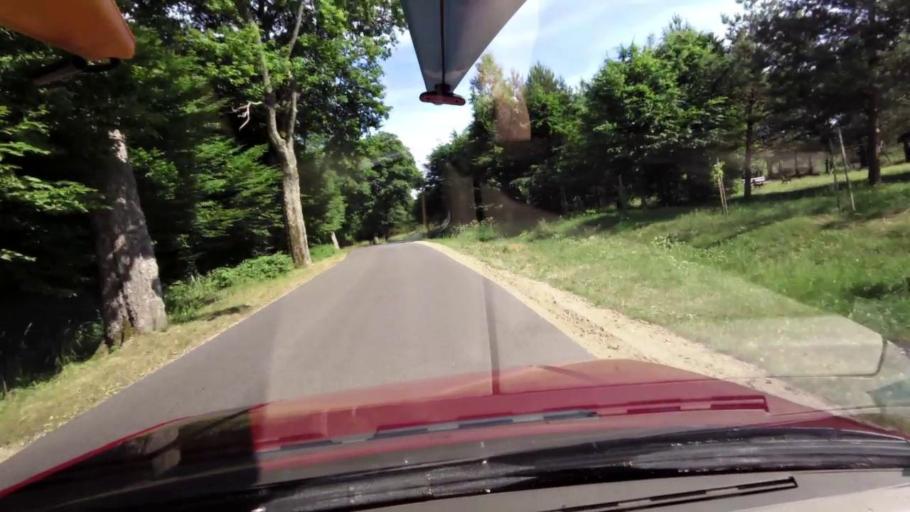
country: PL
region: Pomeranian Voivodeship
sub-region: Powiat slupski
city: Kepice
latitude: 54.1493
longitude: 16.9101
